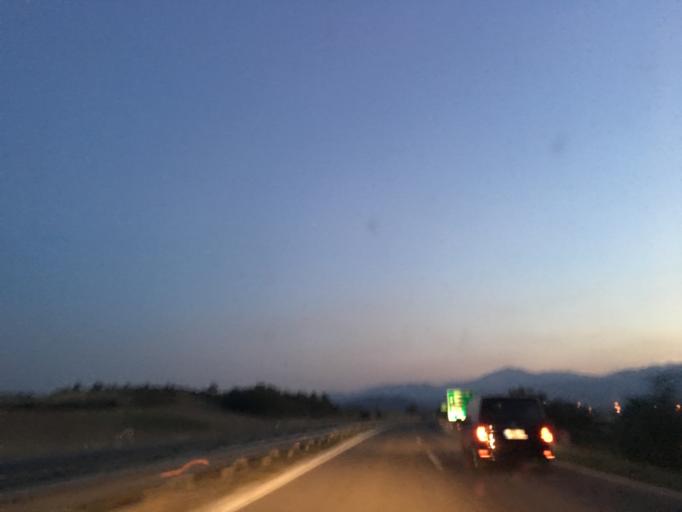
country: MK
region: Petrovec
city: Petrovec
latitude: 41.9465
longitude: 21.6305
